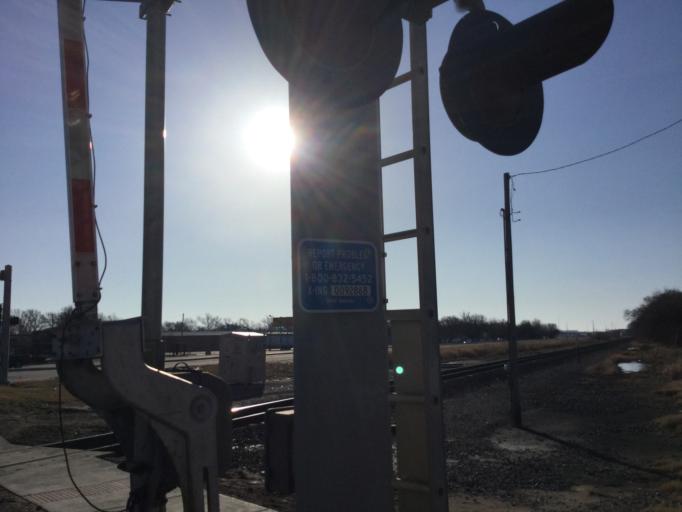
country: US
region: Kansas
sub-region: Sedgwick County
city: Wichita
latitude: 37.6498
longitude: -97.3161
